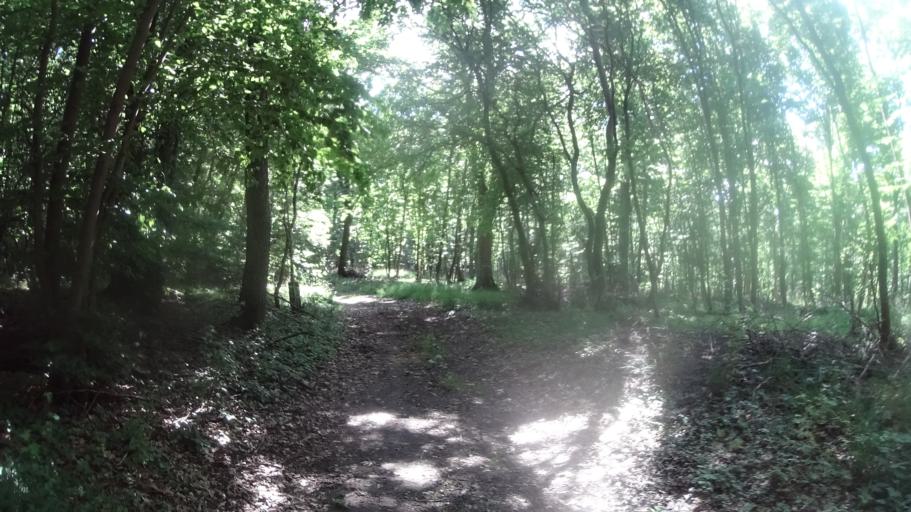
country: DE
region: Lower Saxony
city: Elbe
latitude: 52.1088
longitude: 10.3048
